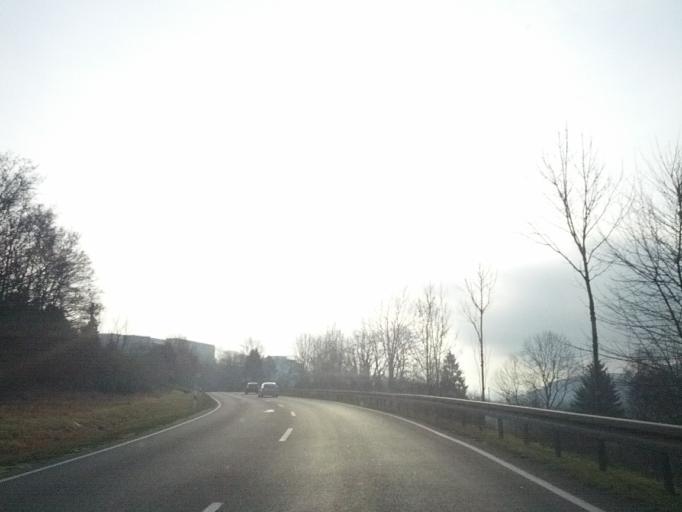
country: DE
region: Thuringia
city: Utendorf
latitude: 50.6010
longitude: 10.4100
